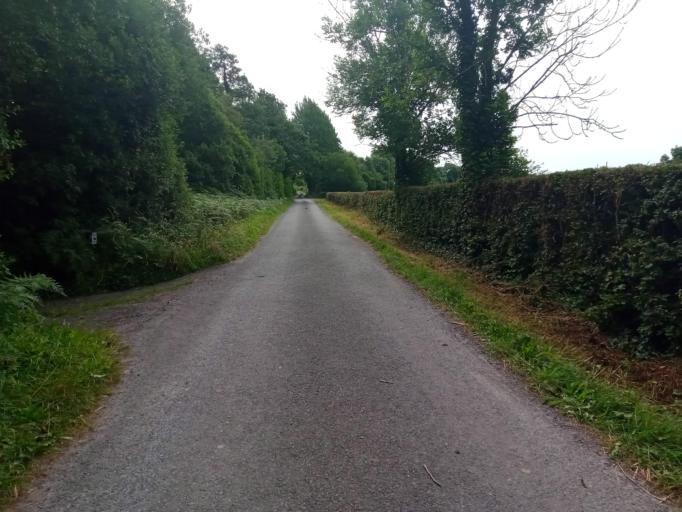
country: IE
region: Leinster
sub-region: Laois
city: Abbeyleix
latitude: 52.8812
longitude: -7.3542
